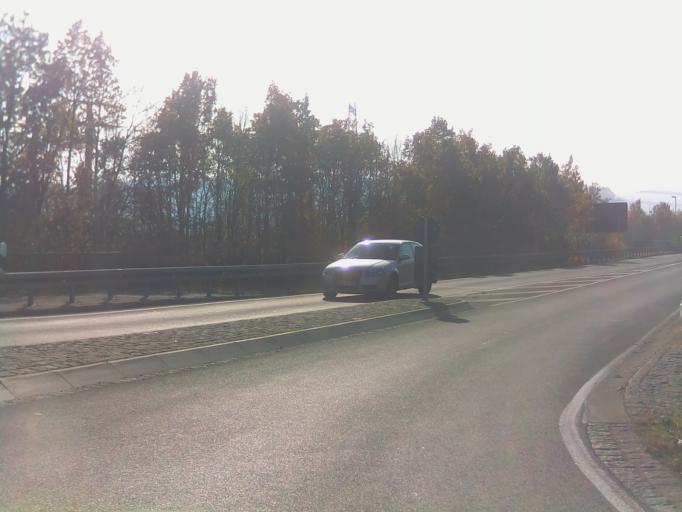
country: DE
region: Bavaria
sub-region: Regierungsbezirk Unterfranken
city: Ebelsbach
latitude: 49.9791
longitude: 10.6715
